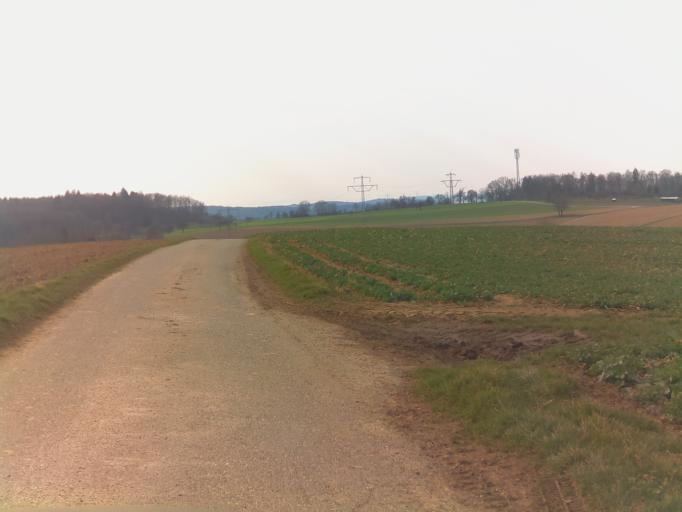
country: DE
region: Baden-Wuerttemberg
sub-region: Karlsruhe Region
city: Eschelbronn
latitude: 49.2955
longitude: 8.8632
